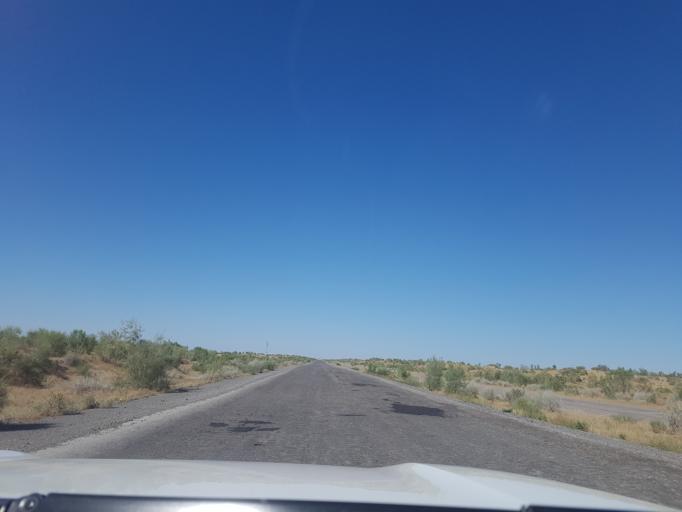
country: TM
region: Lebap
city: Turkmenabat
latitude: 38.3410
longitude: 63.0164
